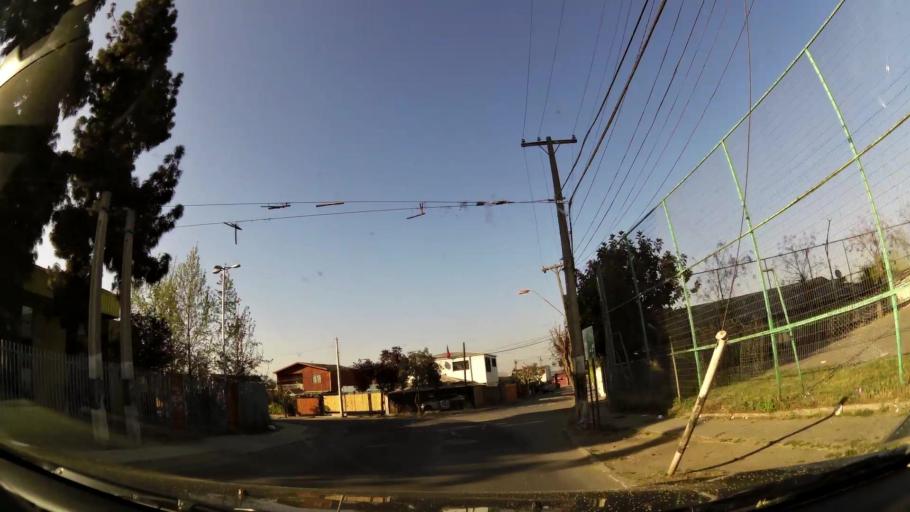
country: CL
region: Santiago Metropolitan
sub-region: Provincia de Santiago
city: Santiago
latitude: -33.3740
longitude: -70.6383
